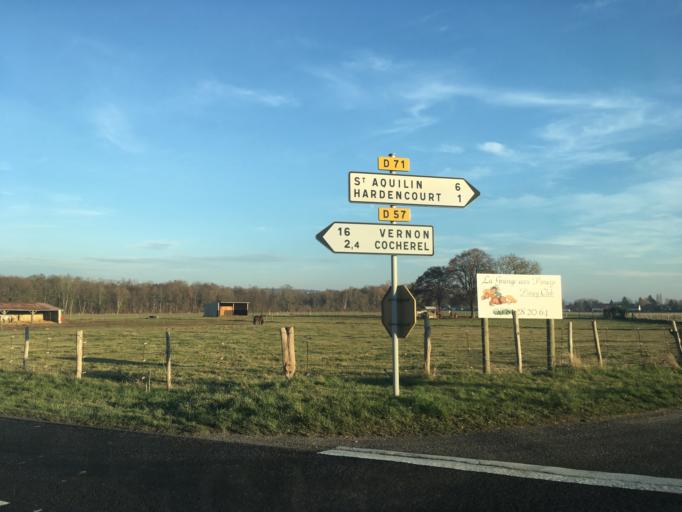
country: FR
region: Haute-Normandie
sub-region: Departement de l'Eure
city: Menilles
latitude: 49.0454
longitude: 1.3089
